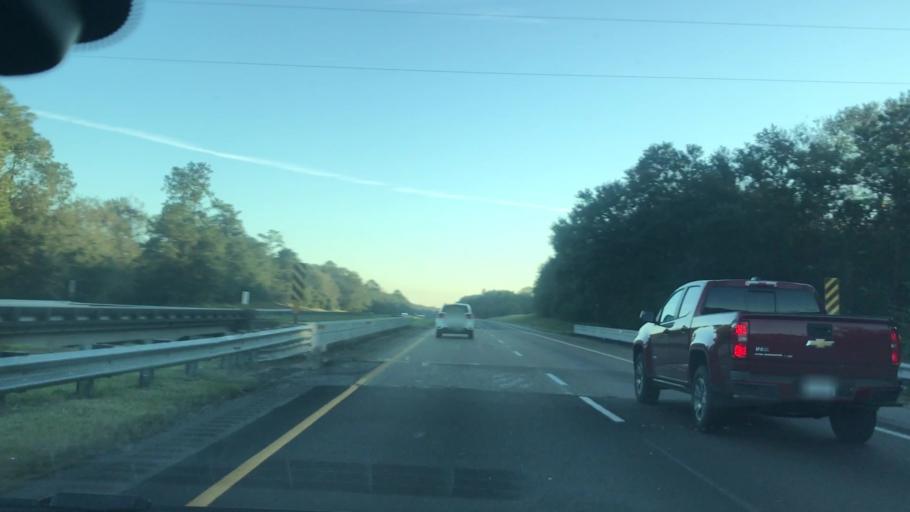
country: US
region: Alabama
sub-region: Mobile County
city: Grand Bay
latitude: 30.5203
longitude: -88.2708
